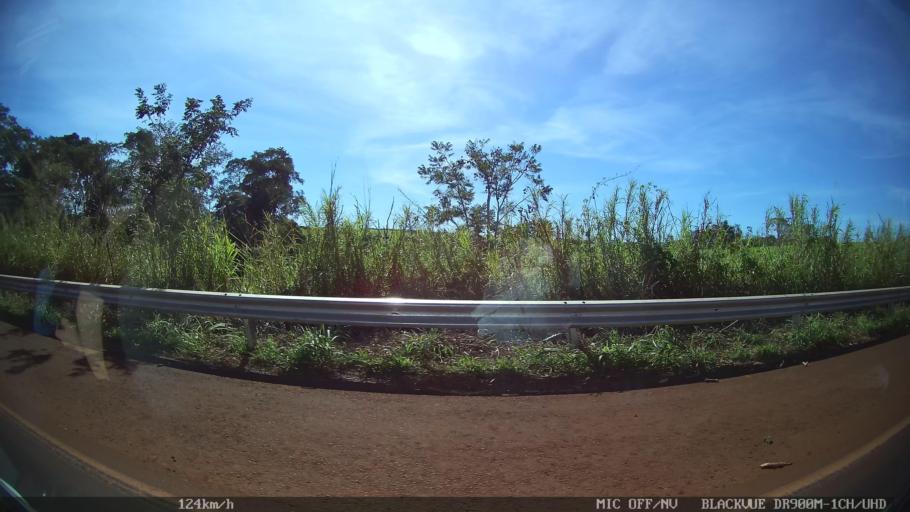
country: BR
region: Sao Paulo
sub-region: Sao Joaquim Da Barra
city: Sao Joaquim da Barra
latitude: -20.5421
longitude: -47.7996
